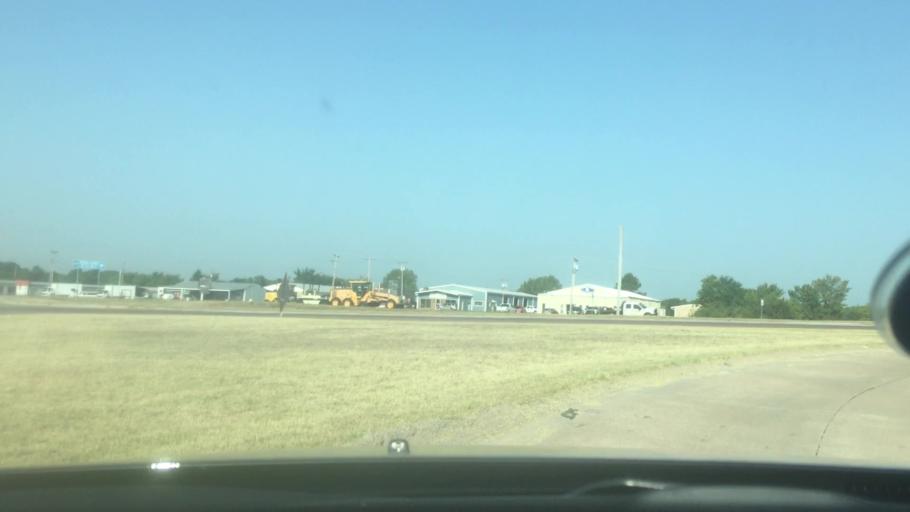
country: US
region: Oklahoma
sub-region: Bryan County
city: Durant
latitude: 34.0219
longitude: -96.3899
